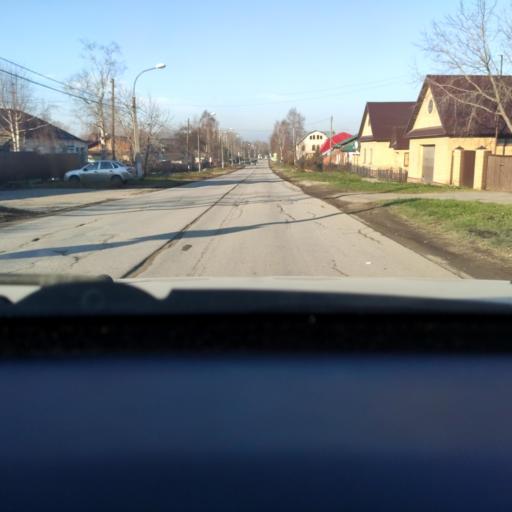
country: RU
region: Perm
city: Perm
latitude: 58.0896
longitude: 56.3901
